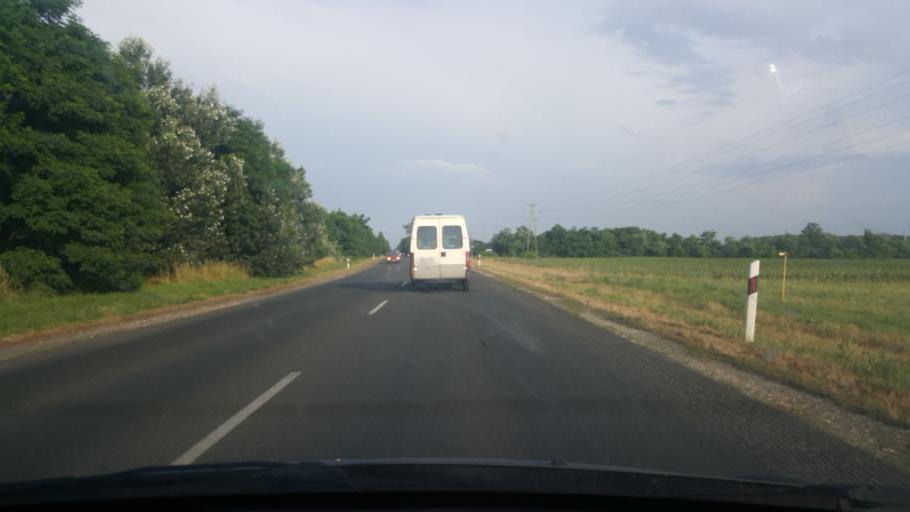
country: HU
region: Pest
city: Peteri
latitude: 47.3620
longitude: 19.3876
